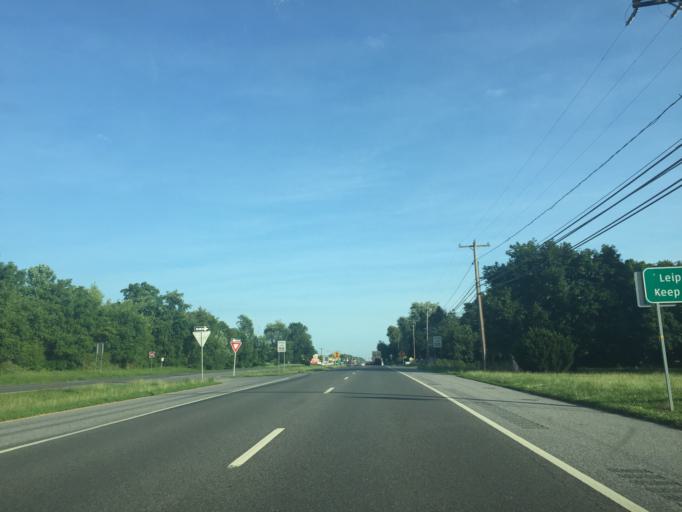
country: US
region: Delaware
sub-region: Kent County
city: Cheswold
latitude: 39.2281
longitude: -75.5787
